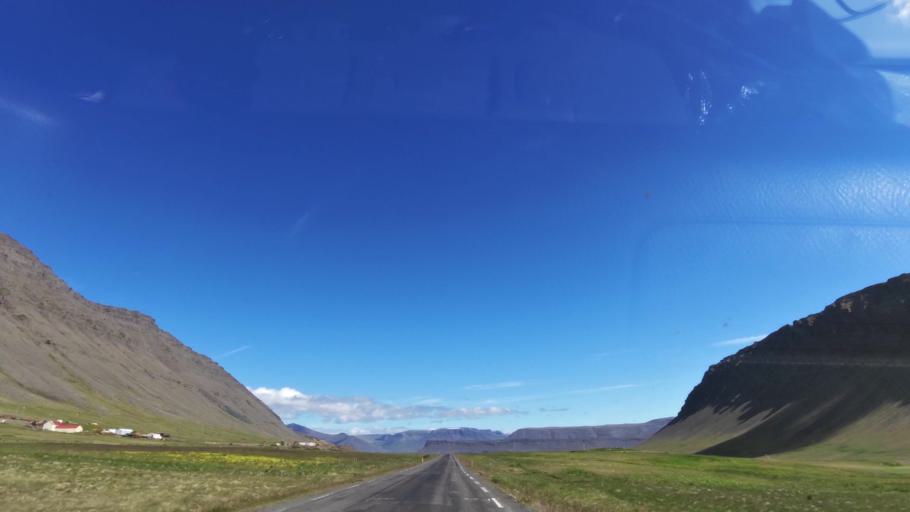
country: IS
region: Westfjords
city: Isafjoerdur
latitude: 65.6694
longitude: -23.6286
